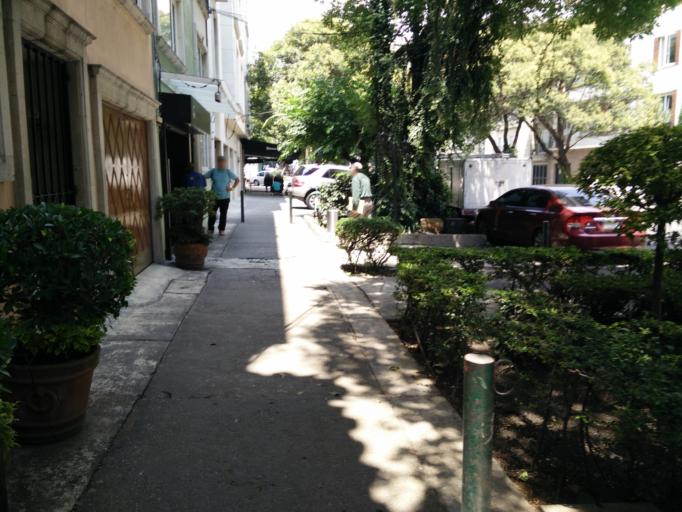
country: MX
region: Mexico City
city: Miguel Hidalgo
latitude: 19.4312
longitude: -99.1918
